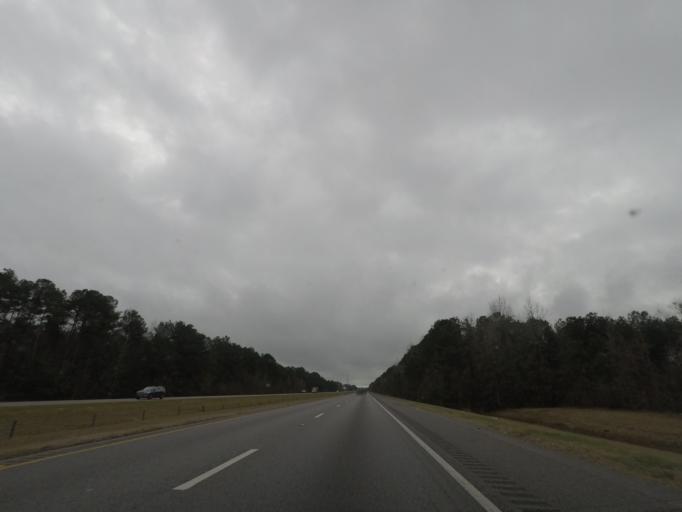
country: US
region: South Carolina
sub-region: Orangeburg County
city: Holly Hill
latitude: 33.4379
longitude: -80.4852
